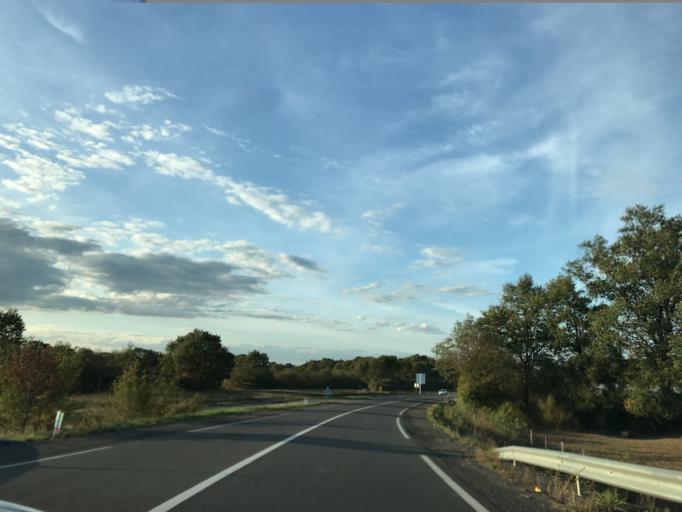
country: FR
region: Auvergne
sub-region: Departement de l'Allier
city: Saint-Yorre
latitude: 46.0466
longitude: 3.4716
